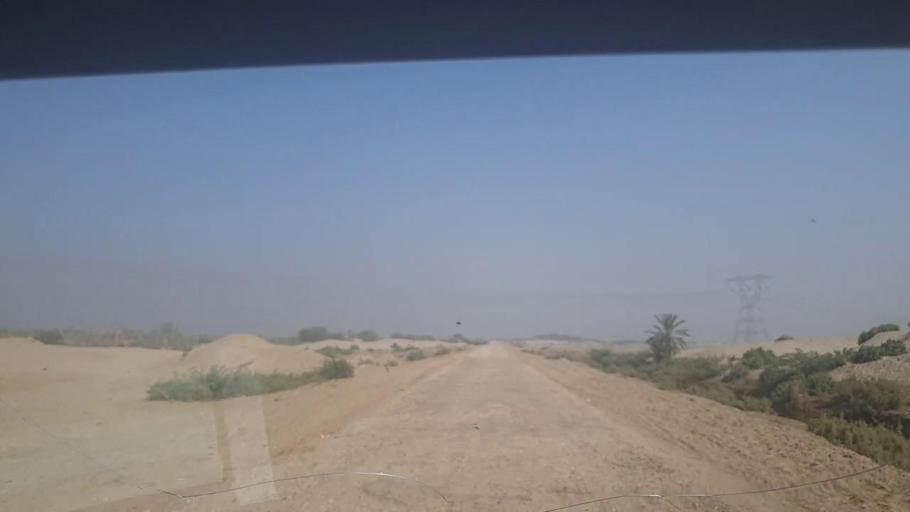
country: PK
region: Sindh
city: Khairpur
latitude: 27.4463
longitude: 68.7181
